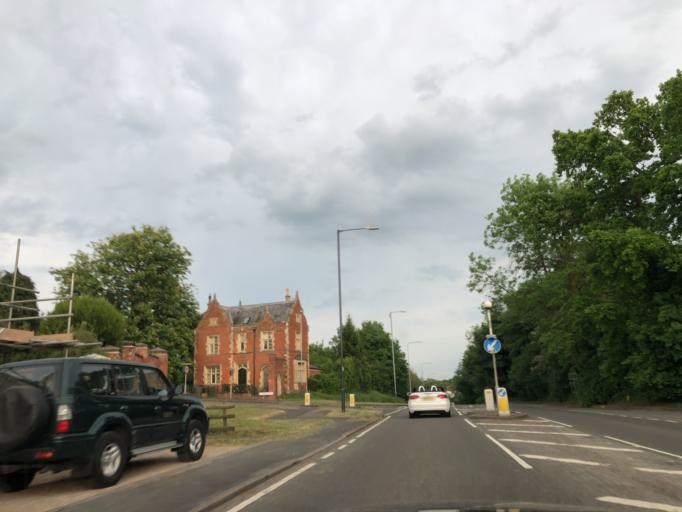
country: GB
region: England
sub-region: Warwickshire
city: Wroxall
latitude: 52.2998
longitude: -1.6381
